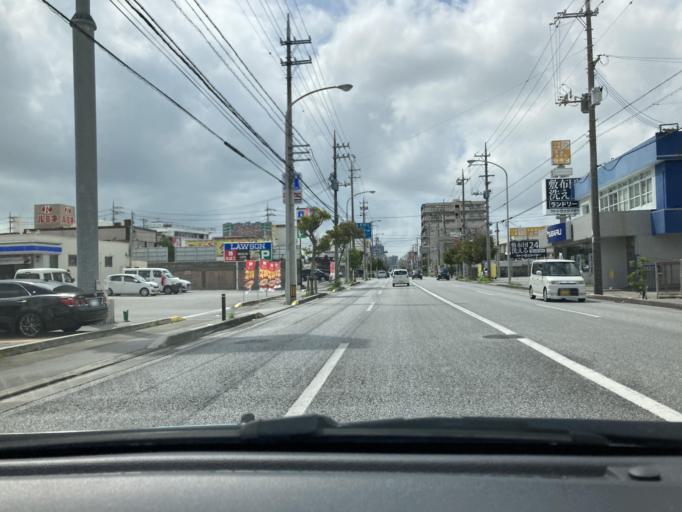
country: JP
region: Okinawa
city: Okinawa
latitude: 26.3505
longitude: 127.8265
